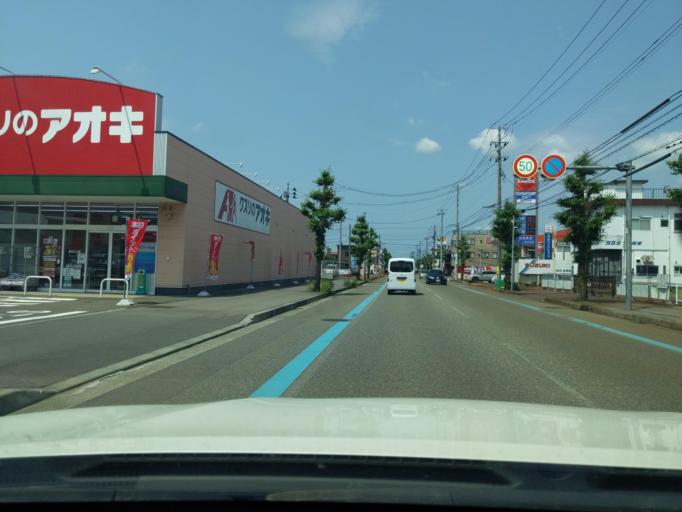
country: JP
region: Niigata
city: Nagaoka
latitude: 37.4276
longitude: 138.8501
